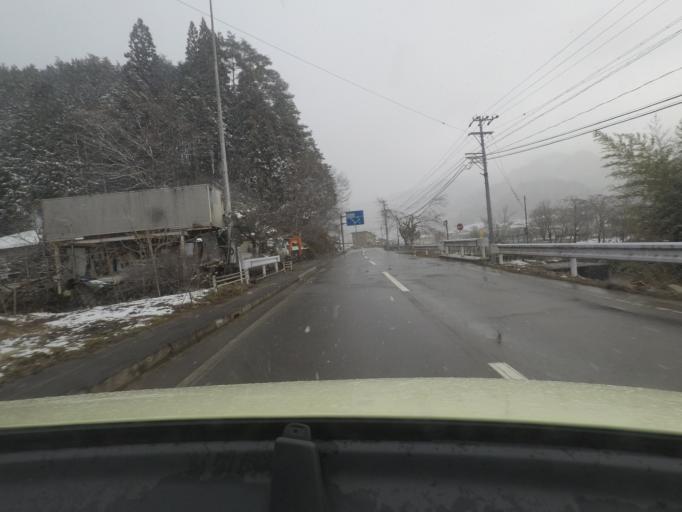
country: JP
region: Gifu
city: Takayama
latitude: 36.1398
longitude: 137.3117
